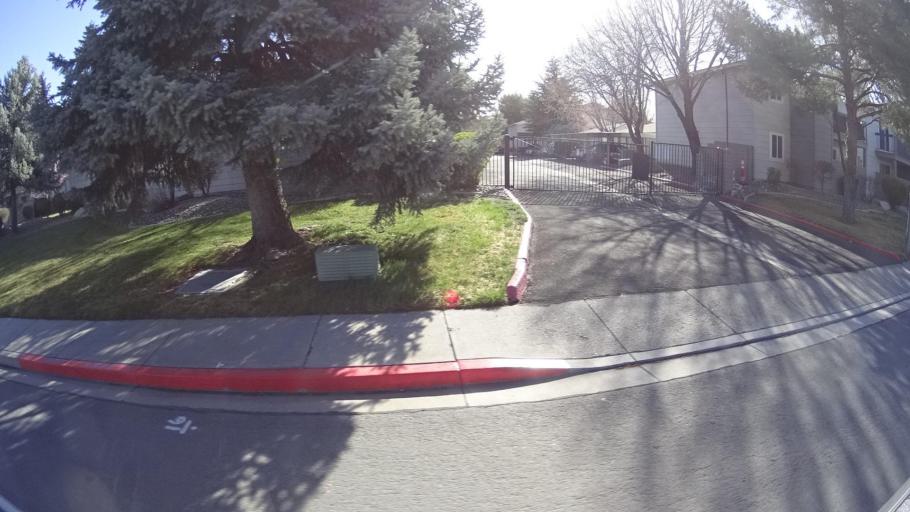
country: US
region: Nevada
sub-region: Washoe County
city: Sparks
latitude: 39.4551
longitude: -119.7745
